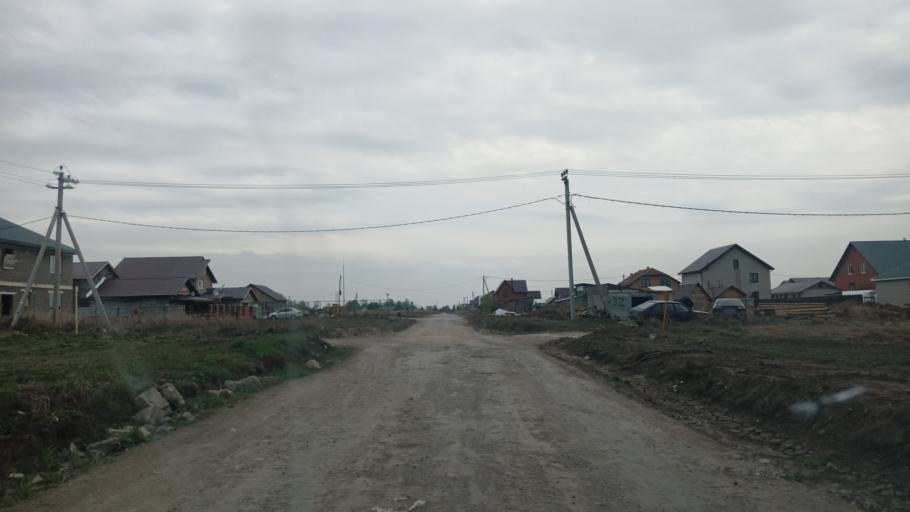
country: RU
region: Altai Krai
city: Yuzhnyy
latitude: 53.2225
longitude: 83.6943
